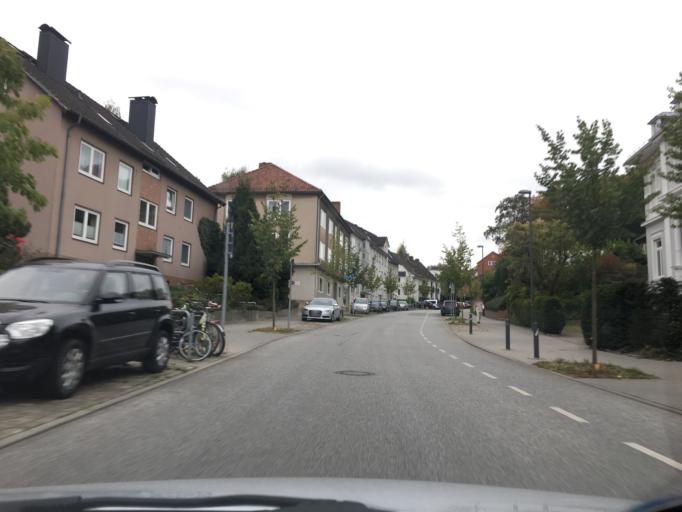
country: DE
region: Schleswig-Holstein
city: Kiel
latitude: 54.3346
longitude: 10.1495
